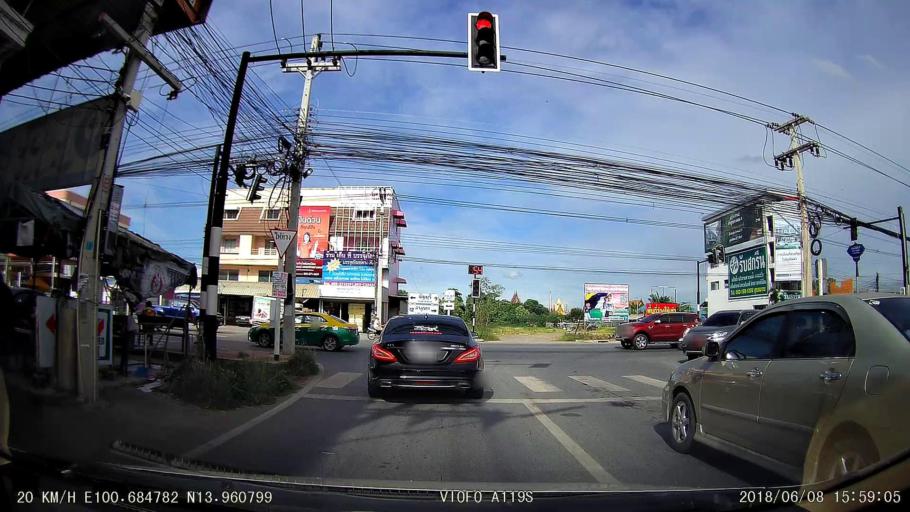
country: TH
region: Bangkok
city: Sai Mai
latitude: 13.9635
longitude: 100.6850
